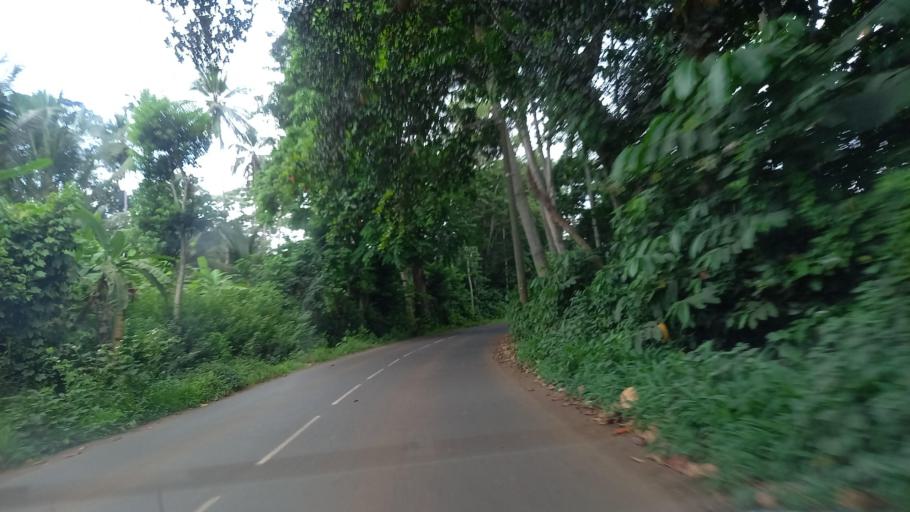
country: YT
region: Ouangani
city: Ouangani
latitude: -12.8303
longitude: 45.1376
